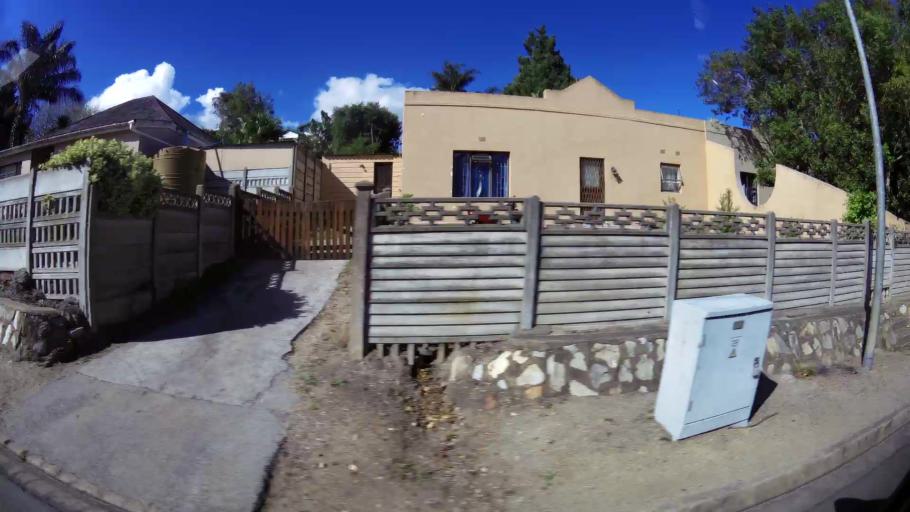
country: ZA
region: Western Cape
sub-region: Eden District Municipality
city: George
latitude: -33.9495
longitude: 22.4719
